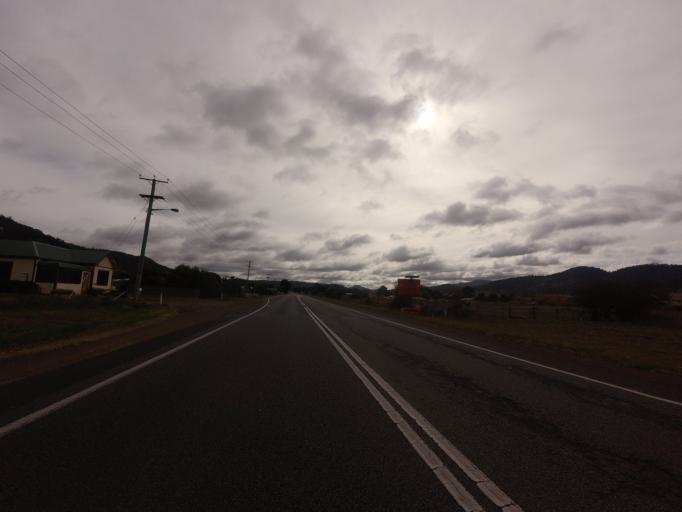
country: AU
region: Tasmania
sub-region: Brighton
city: Bridgewater
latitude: -42.6555
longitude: 147.2425
